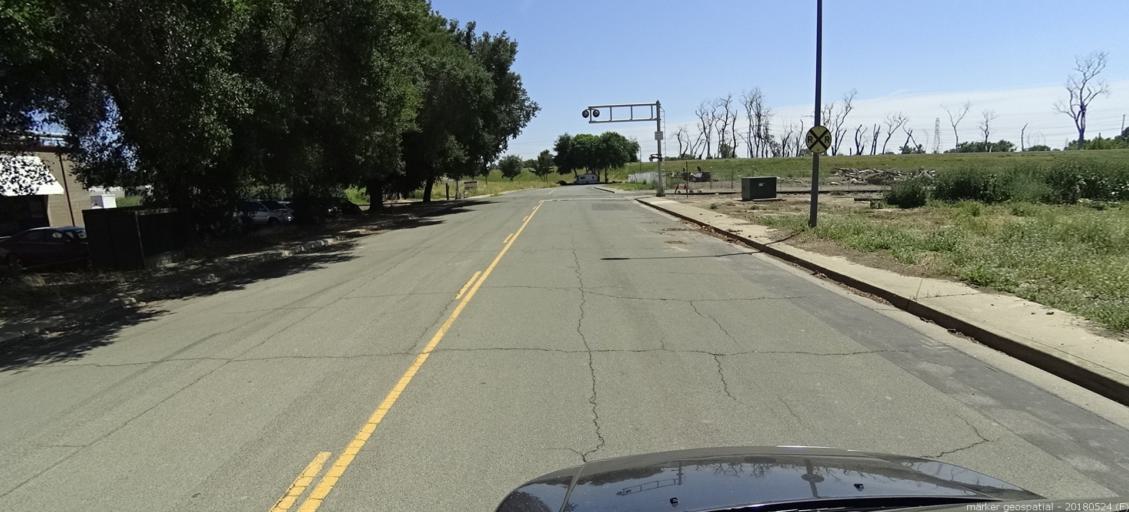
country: US
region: California
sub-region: Sacramento County
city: Sacramento
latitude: 38.5968
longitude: -121.4655
